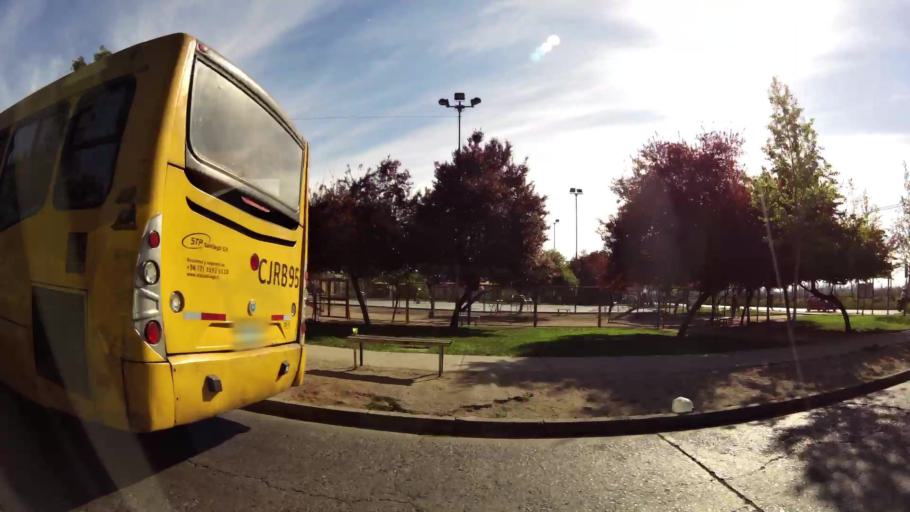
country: CL
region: Santiago Metropolitan
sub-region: Provincia de Cordillera
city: Puente Alto
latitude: -33.6052
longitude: -70.5930
